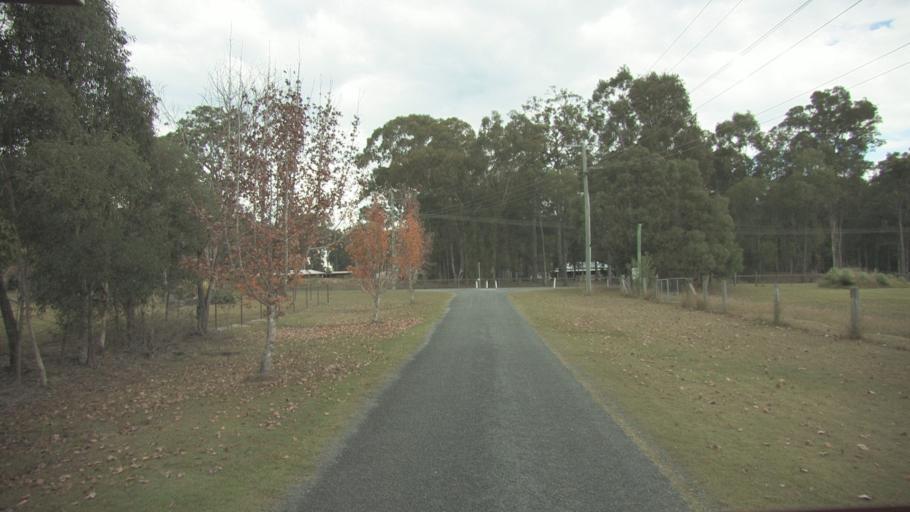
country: AU
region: Queensland
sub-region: Logan
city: Chambers Flat
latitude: -27.7831
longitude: 153.1124
